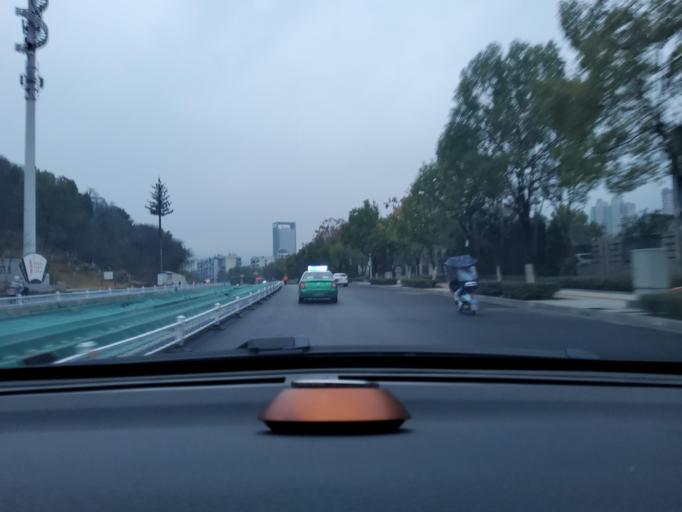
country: CN
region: Hubei
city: Tuanchengshan
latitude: 30.1936
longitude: 115.0238
